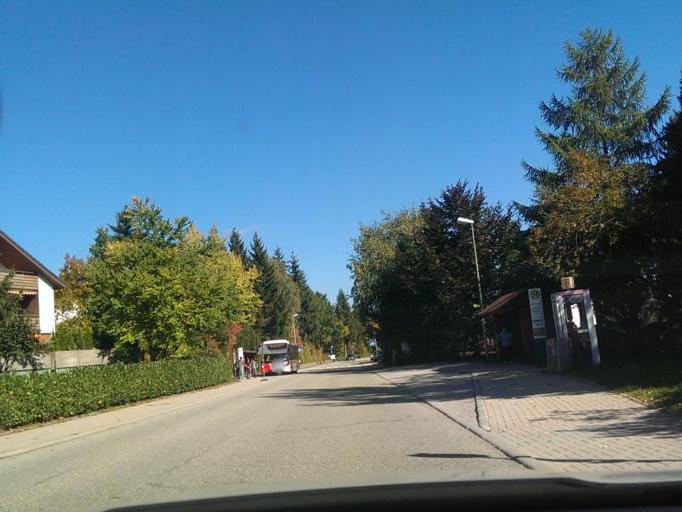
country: DE
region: Baden-Wuerttemberg
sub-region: Karlsruhe Region
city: Dobel
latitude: 48.8000
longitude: 8.5019
